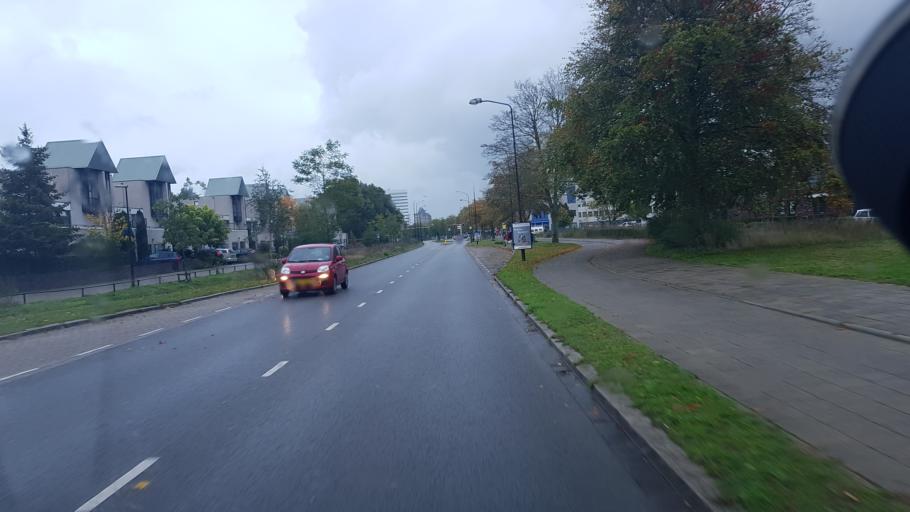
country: NL
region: Gelderland
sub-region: Gemeente Apeldoorn
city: Apeldoorn
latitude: 52.2081
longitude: 5.9535
